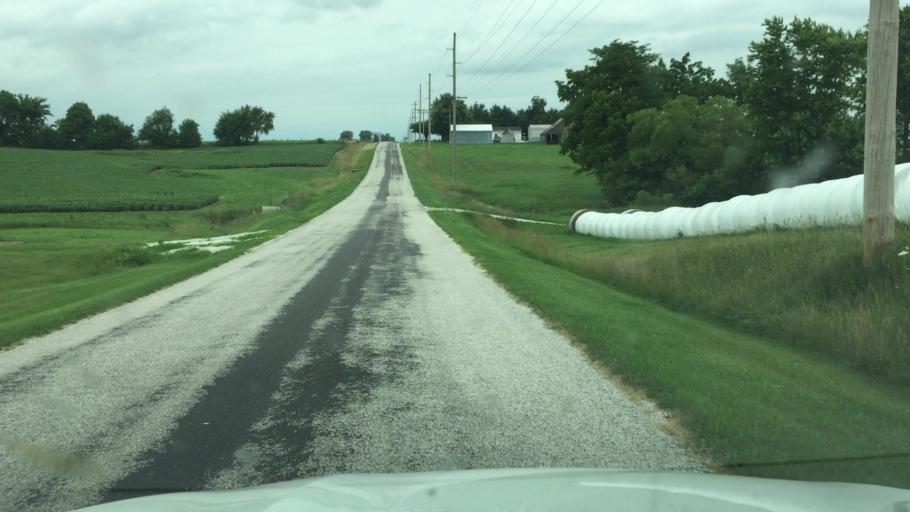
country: US
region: Illinois
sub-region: Hancock County
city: Carthage
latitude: 40.2991
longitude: -91.0832
